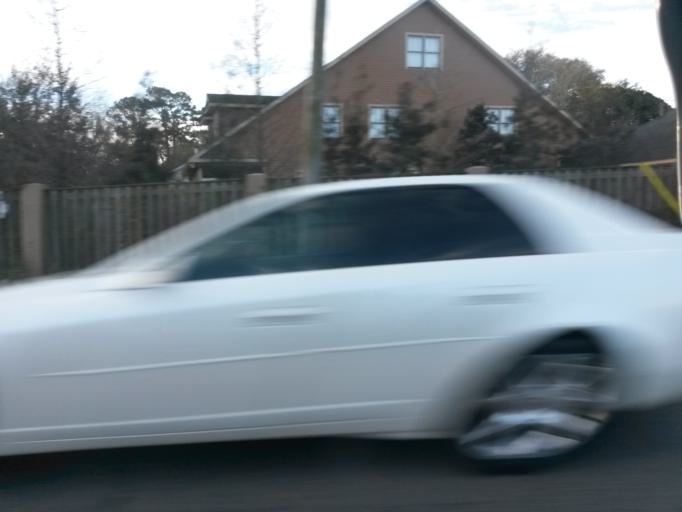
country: US
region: Louisiana
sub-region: Lafayette Parish
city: Lafayette
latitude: 30.2324
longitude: -92.0376
